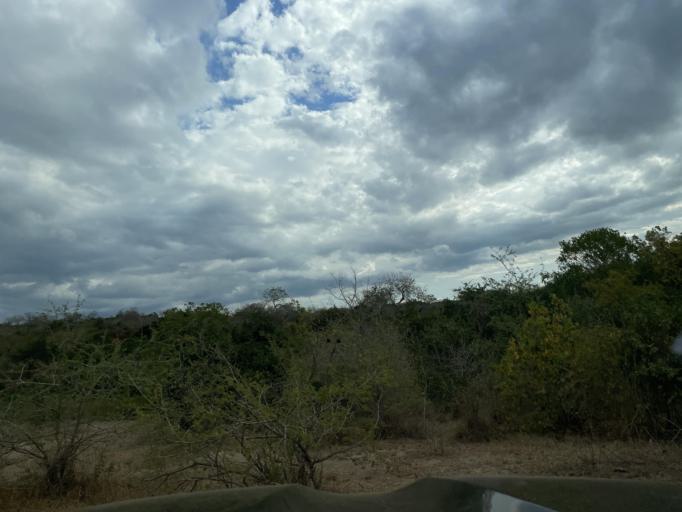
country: TZ
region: Pwani
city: Mvomero
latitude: -6.0100
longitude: 38.4210
